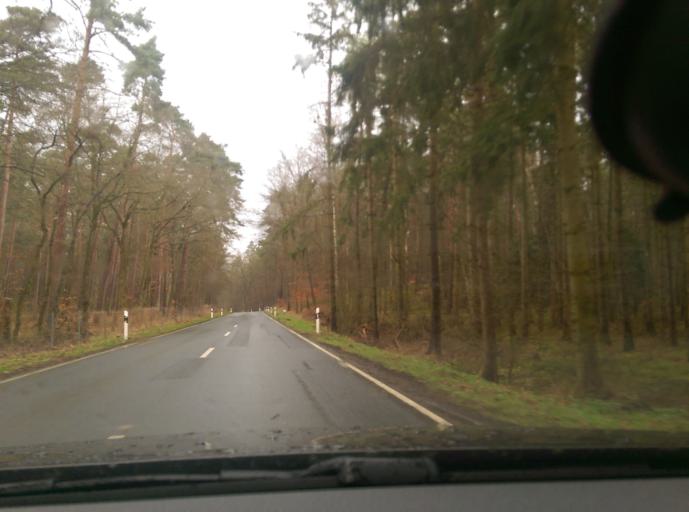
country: DE
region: Lower Saxony
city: Schwarmstedt
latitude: 52.6480
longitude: 9.6137
